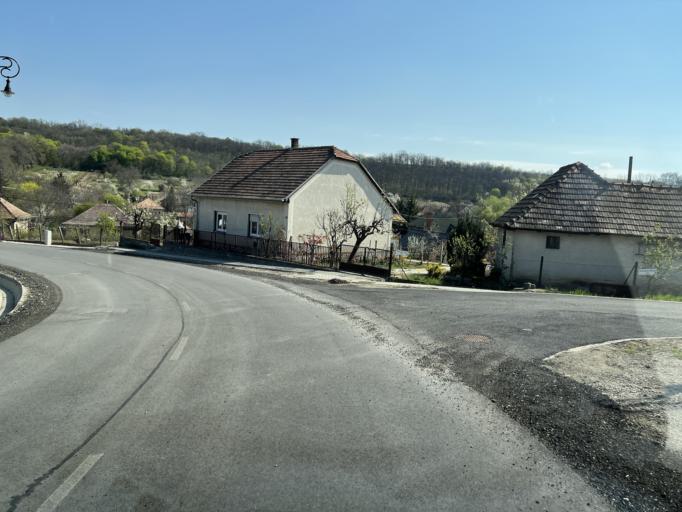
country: HU
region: Pest
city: Orbottyan
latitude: 47.7359
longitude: 19.2897
